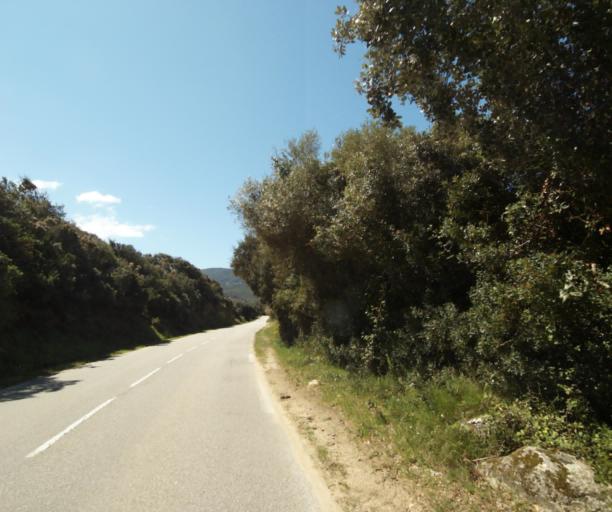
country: FR
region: Corsica
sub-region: Departement de la Corse-du-Sud
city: Propriano
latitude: 41.6481
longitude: 8.8773
